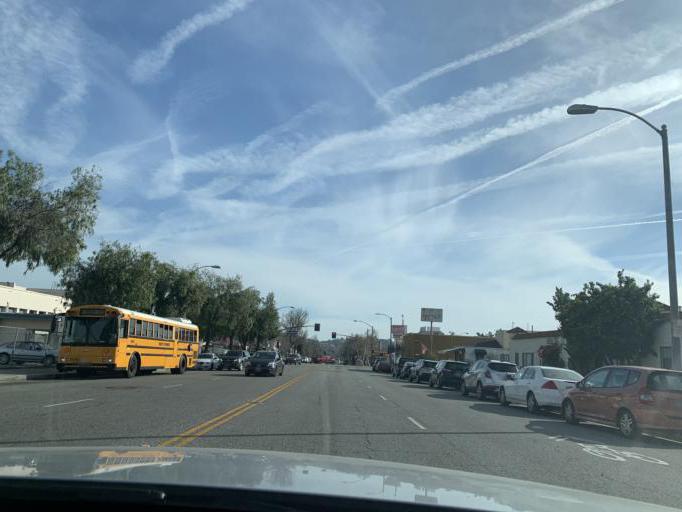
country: US
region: California
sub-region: Los Angeles County
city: Glendale
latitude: 34.1474
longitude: -118.2397
